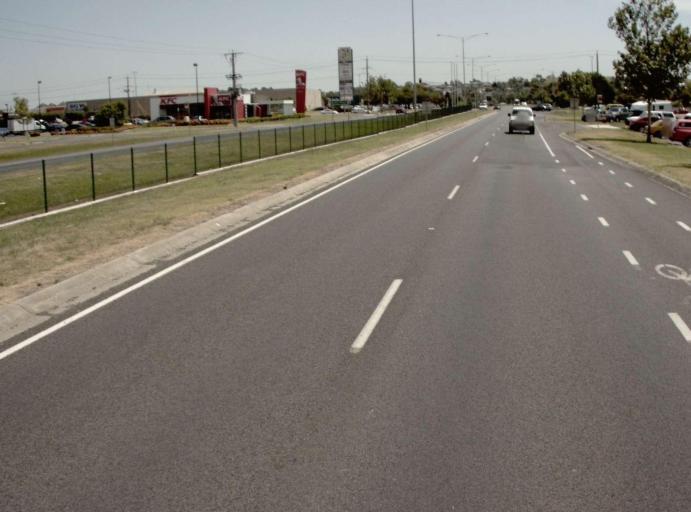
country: AU
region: Victoria
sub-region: Latrobe
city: Morwell
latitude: -38.2342
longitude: 146.4337
